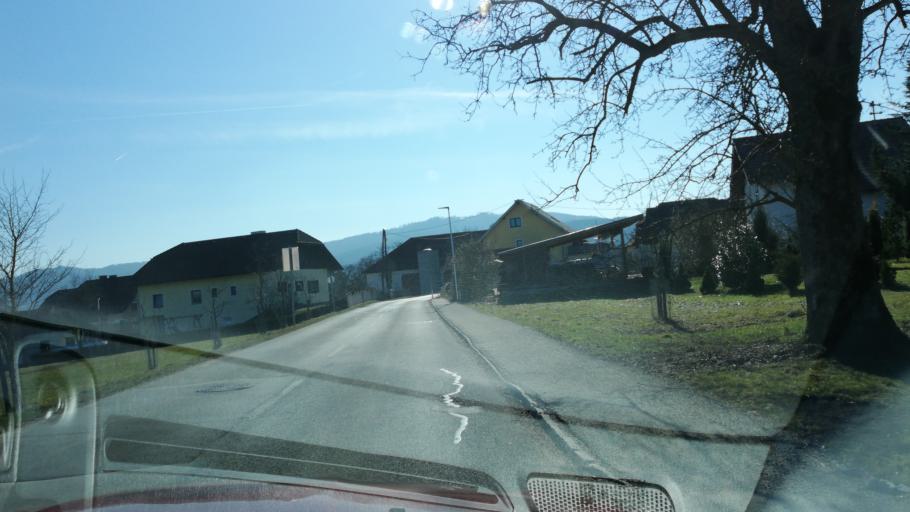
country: AT
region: Upper Austria
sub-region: Politischer Bezirk Vocklabruck
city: Lenzing
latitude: 47.9624
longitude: 13.6342
